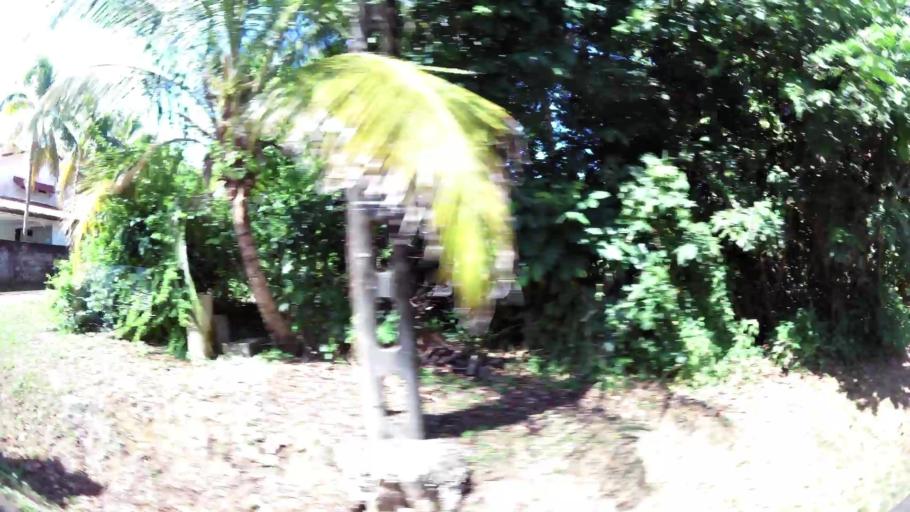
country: GF
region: Guyane
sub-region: Guyane
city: Remire-Montjoly
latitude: 4.9231
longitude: -52.2790
